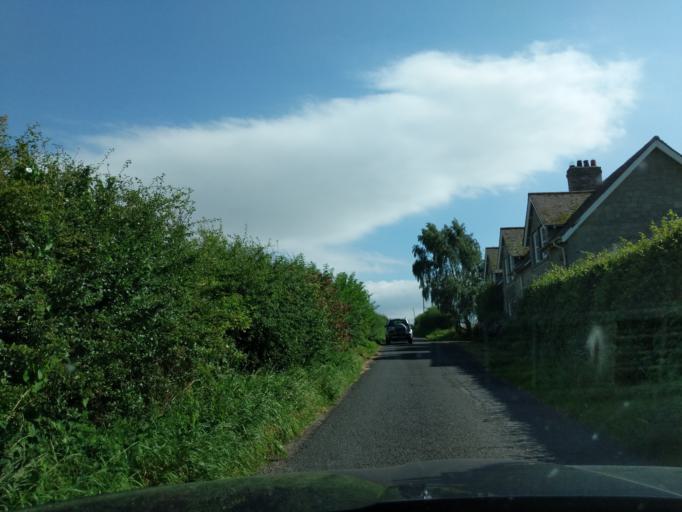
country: GB
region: England
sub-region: Northumberland
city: Ford
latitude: 55.6584
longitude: -2.1527
